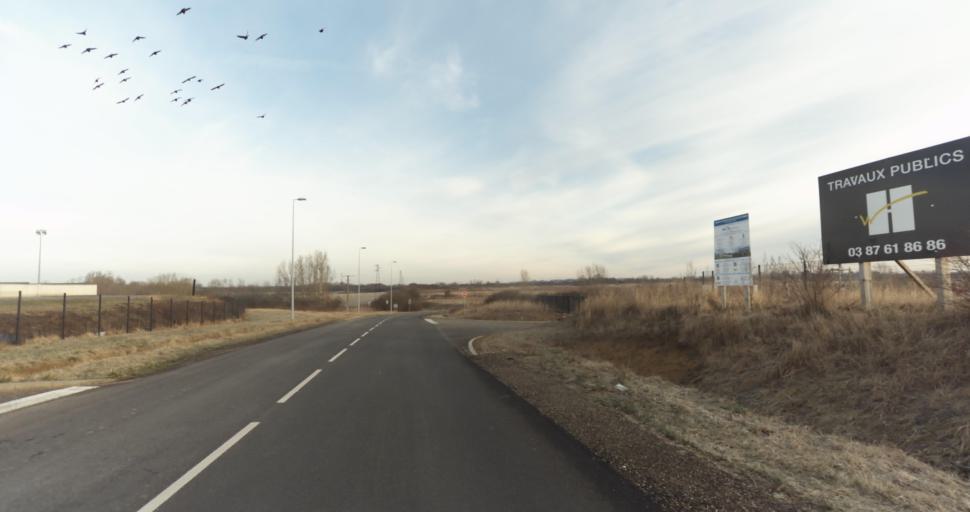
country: FR
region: Lorraine
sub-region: Departement de Meurthe-et-Moselle
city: Giraumont
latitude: 49.1584
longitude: 5.9032
